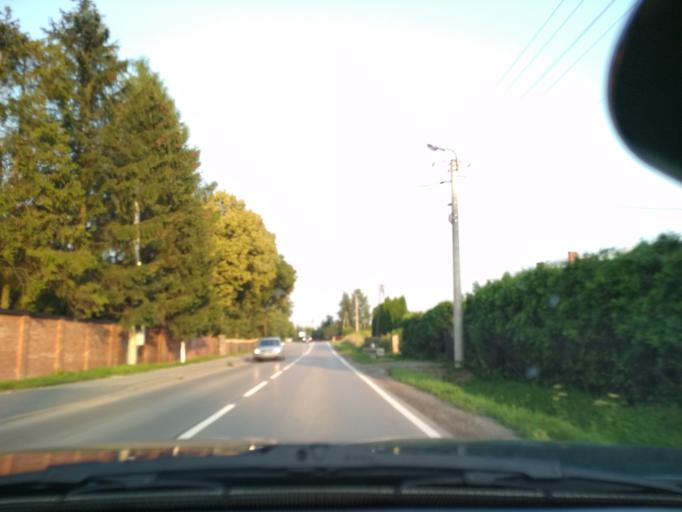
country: PL
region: Lesser Poland Voivodeship
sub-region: Powiat olkuski
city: Wolbrom
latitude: 50.3933
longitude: 19.7446
